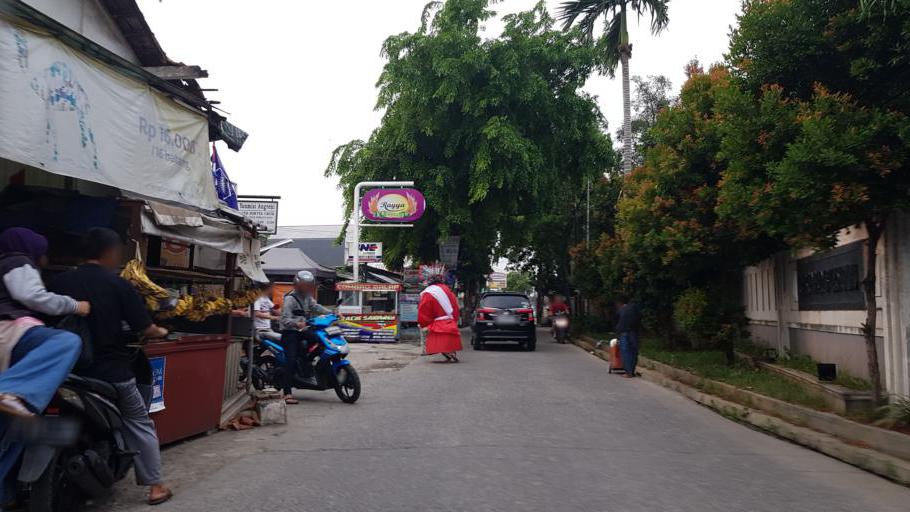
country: ID
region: West Java
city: Depok
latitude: -6.3745
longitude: 106.8011
